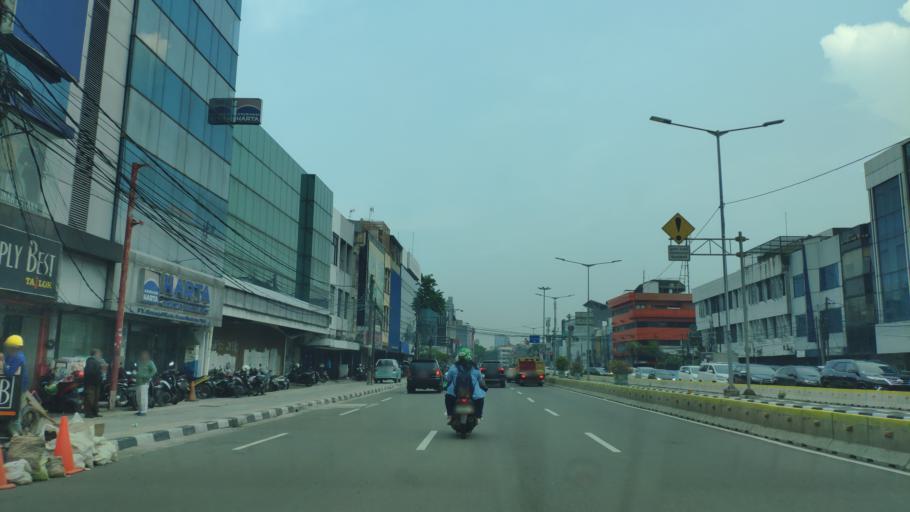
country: ID
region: Jakarta Raya
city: Jakarta
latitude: -6.1705
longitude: 106.8137
